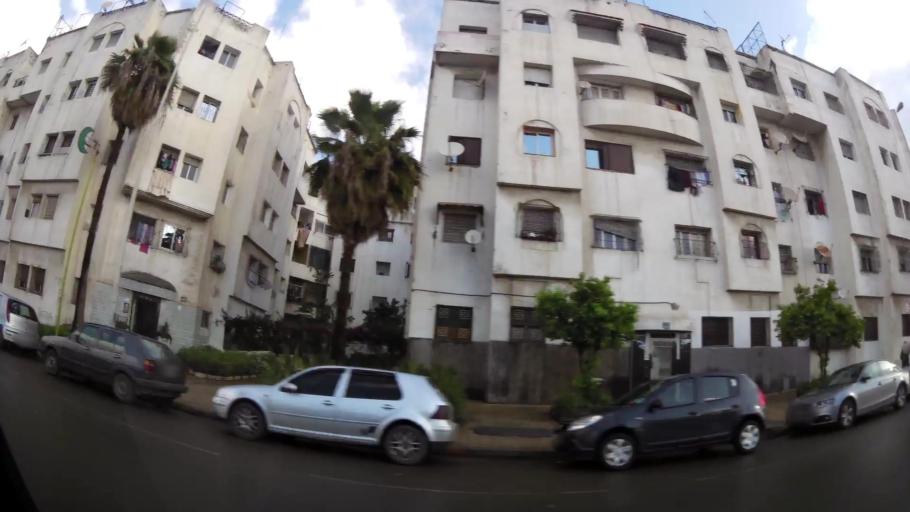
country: MA
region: Grand Casablanca
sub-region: Mediouna
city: Tit Mellil
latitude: 33.5973
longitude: -7.5223
